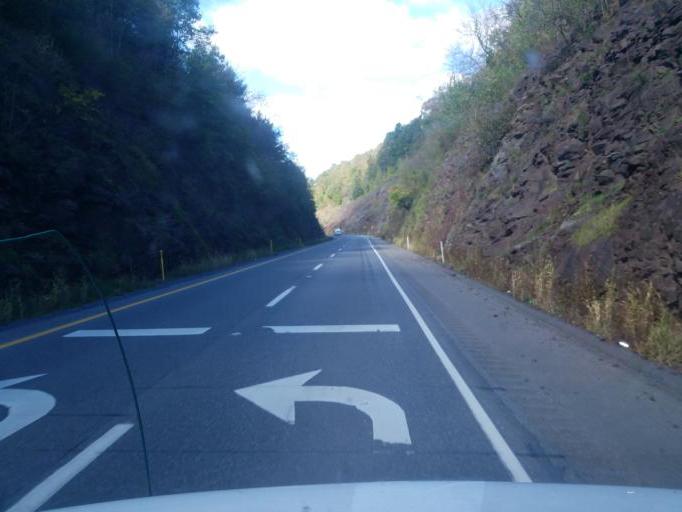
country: US
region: Pennsylvania
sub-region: Bedford County
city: Earlston
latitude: 39.9970
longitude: -78.2618
